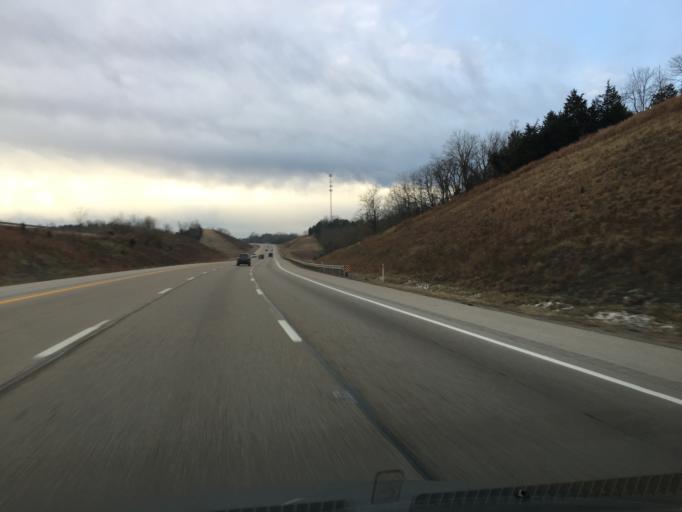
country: US
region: Kentucky
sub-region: Grant County
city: Williamstown
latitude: 38.5665
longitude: -84.5940
